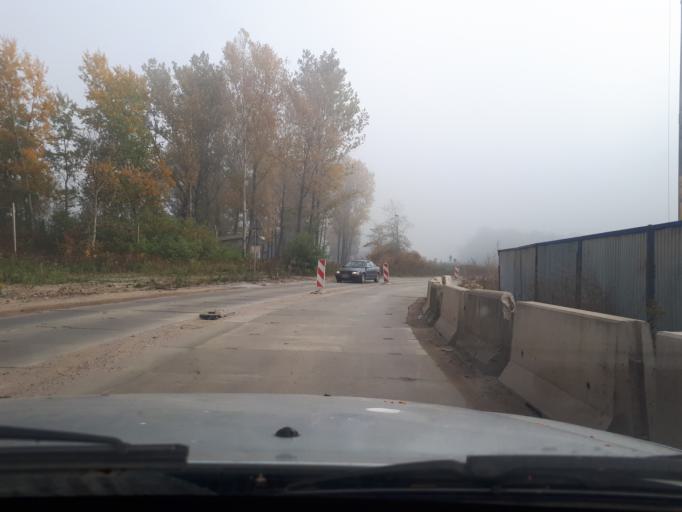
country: PL
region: Lesser Poland Voivodeship
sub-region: Powiat wielicki
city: Wegrzce Wielkie
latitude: 50.0745
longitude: 20.1327
